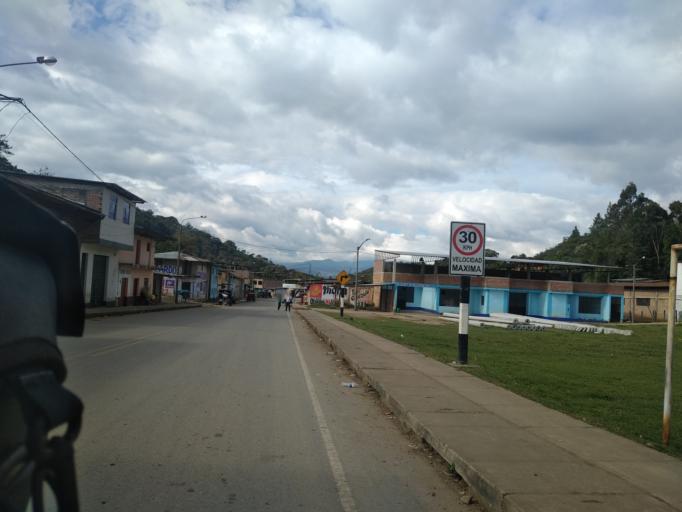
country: PE
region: Cajamarca
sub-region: Provincia de San Ignacio
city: San Ignacio
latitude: -5.0994
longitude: -79.0467
